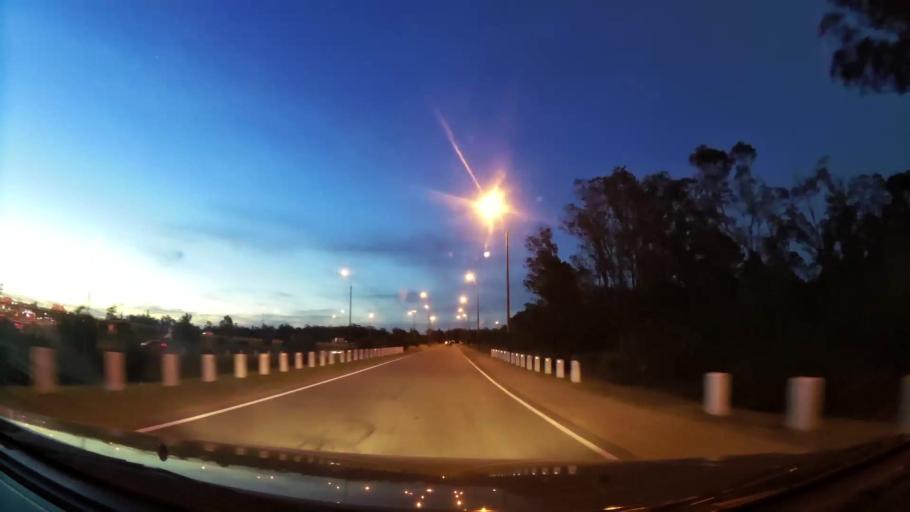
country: UY
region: Canelones
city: Atlantida
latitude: -34.7660
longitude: -55.7625
